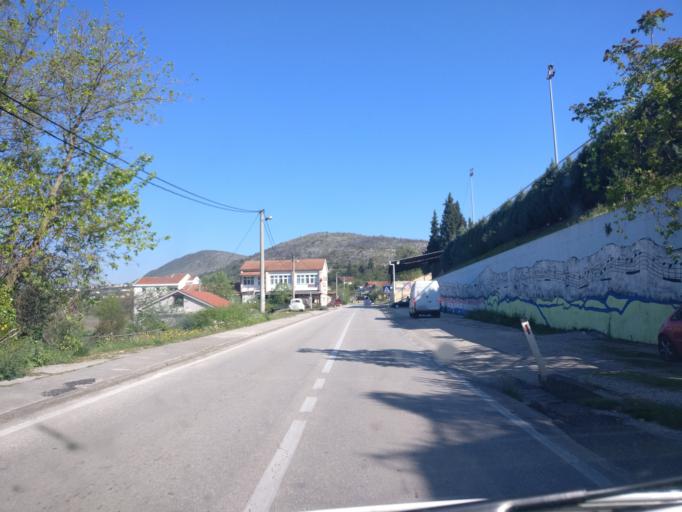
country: BA
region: Federation of Bosnia and Herzegovina
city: Capljina
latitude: 43.1318
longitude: 17.6759
